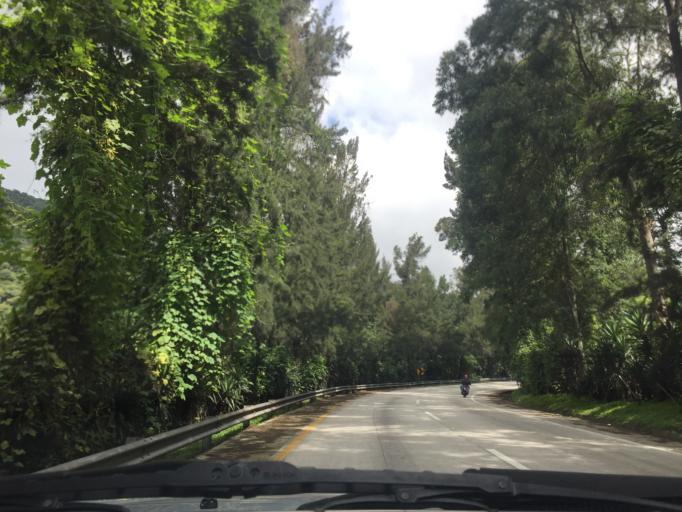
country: GT
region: Sacatepequez
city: Santa Lucia Milpas Altas
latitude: 14.5595
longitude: -90.7022
